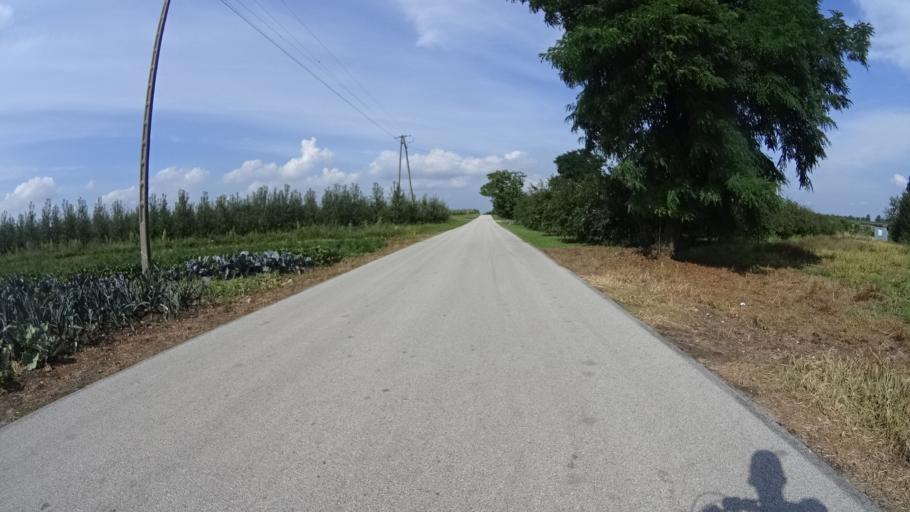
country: PL
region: Masovian Voivodeship
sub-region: Powiat grojecki
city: Goszczyn
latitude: 51.6914
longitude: 20.8458
